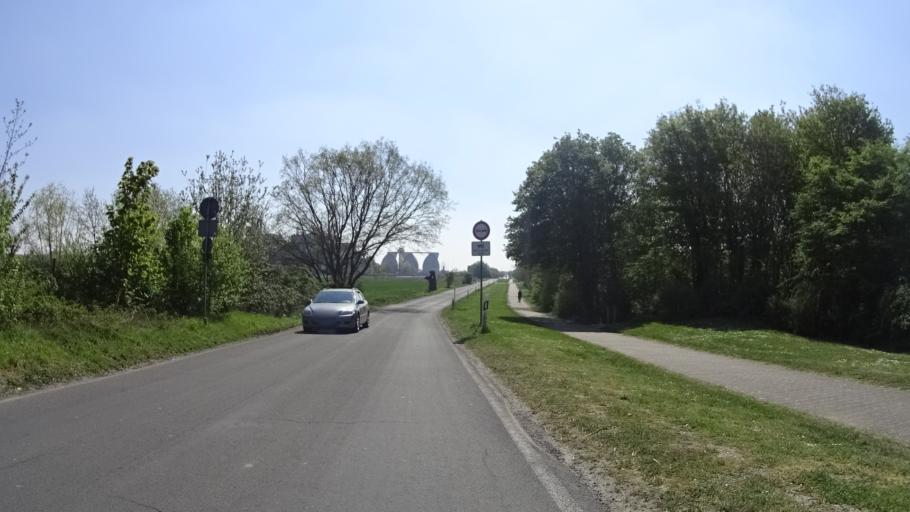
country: DE
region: North Rhine-Westphalia
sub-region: Regierungsbezirk Dusseldorf
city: Krefeld
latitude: 51.3855
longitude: 6.6322
